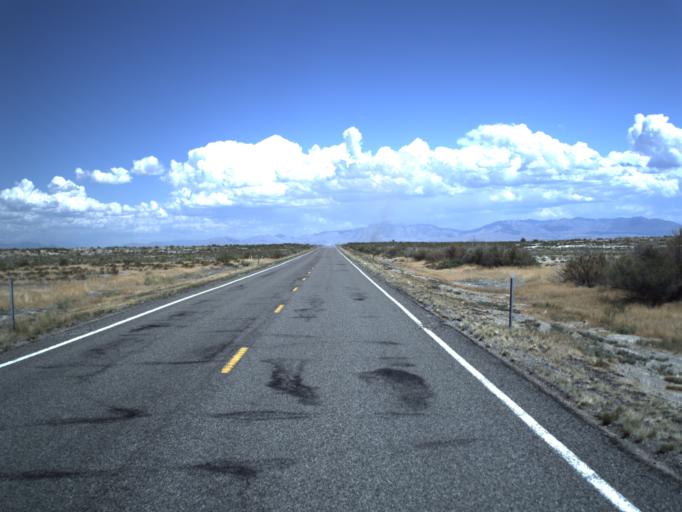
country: US
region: Utah
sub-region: Millard County
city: Delta
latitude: 39.3058
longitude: -112.7979
